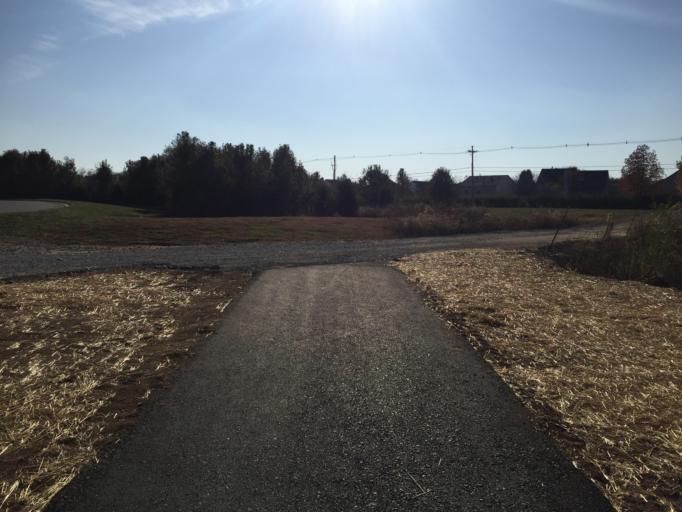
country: US
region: Kentucky
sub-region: Jefferson County
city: Worthington
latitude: 38.3289
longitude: -85.5728
